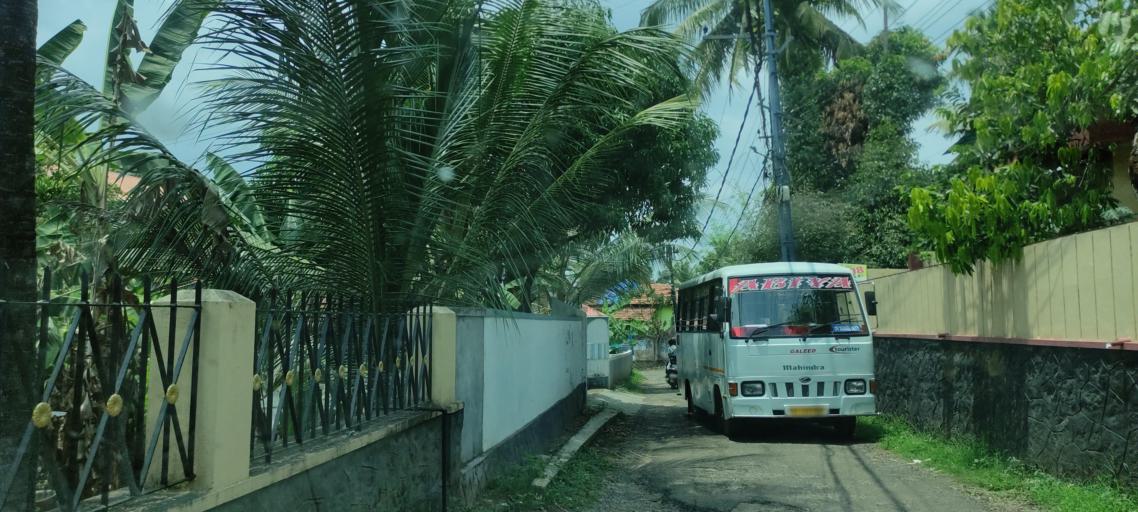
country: IN
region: Kerala
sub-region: Pattanamtitta
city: Adur
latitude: 9.1527
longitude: 76.7297
